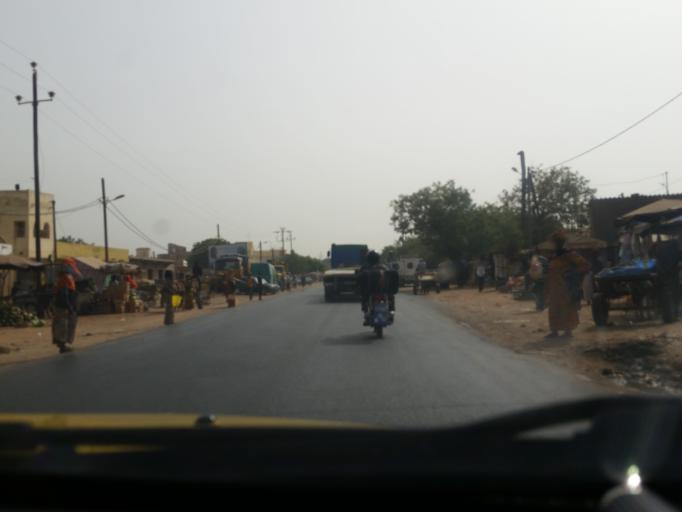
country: SN
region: Thies
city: Pout
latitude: 14.7452
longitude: -17.1343
